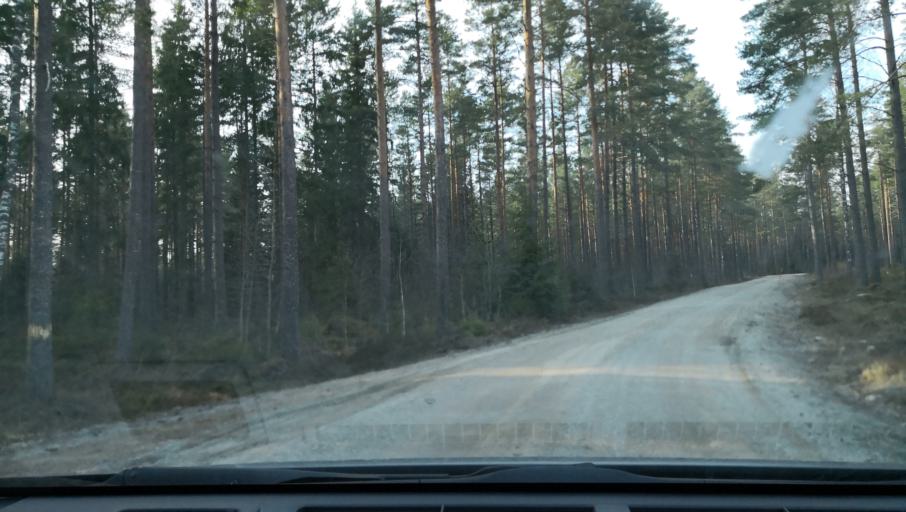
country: SE
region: OErebro
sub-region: Orebro Kommun
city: Hovsta
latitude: 59.3595
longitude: 15.3289
